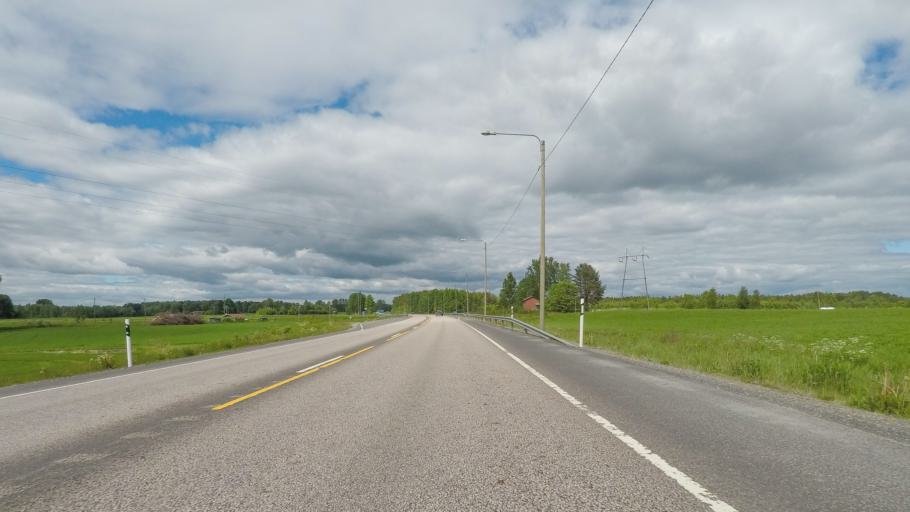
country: FI
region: Paijanne Tavastia
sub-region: Lahti
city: Hartola
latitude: 61.6048
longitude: 26.0090
